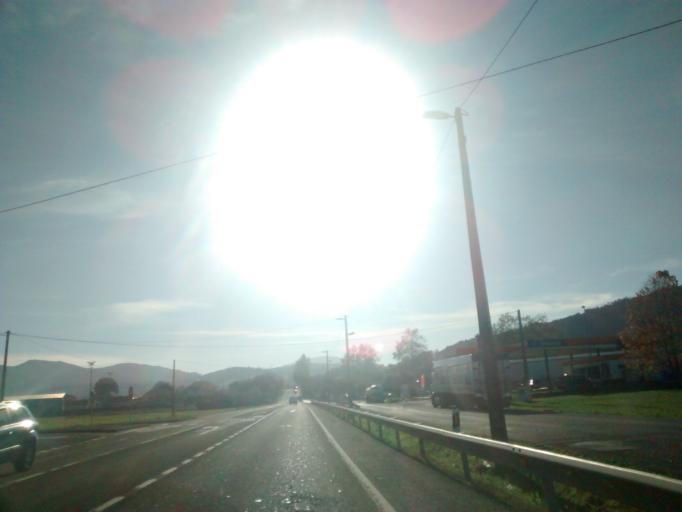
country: ES
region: Cantabria
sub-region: Provincia de Cantabria
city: Puente Viesgo
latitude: 43.3288
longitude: -3.9679
